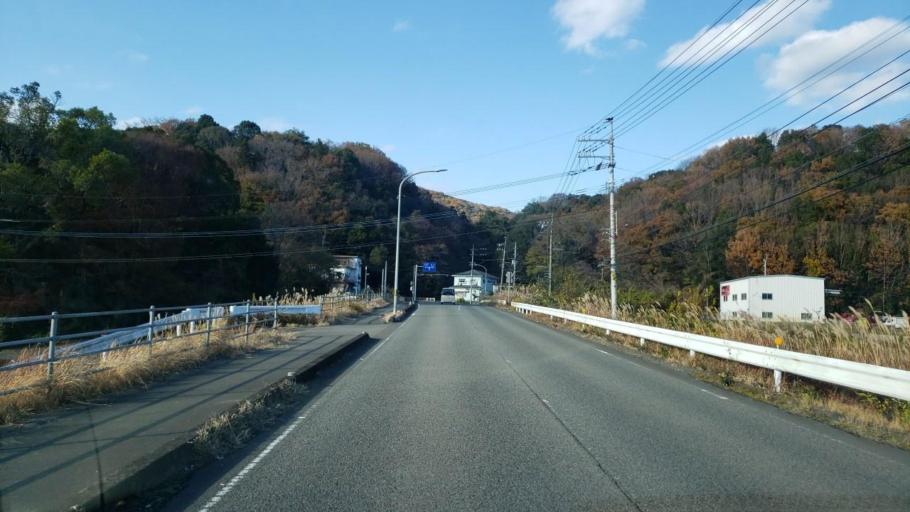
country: JP
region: Tokushima
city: Wakimachi
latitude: 34.0593
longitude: 134.0810
